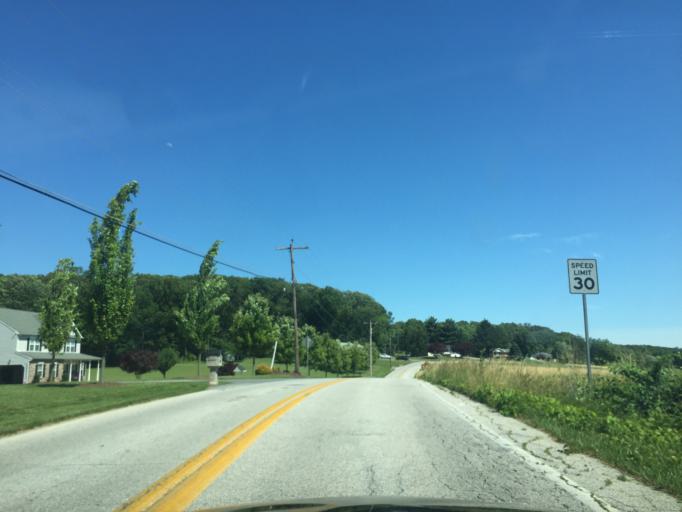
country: US
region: Maryland
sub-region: Carroll County
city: Manchester
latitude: 39.6277
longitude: -76.9321
